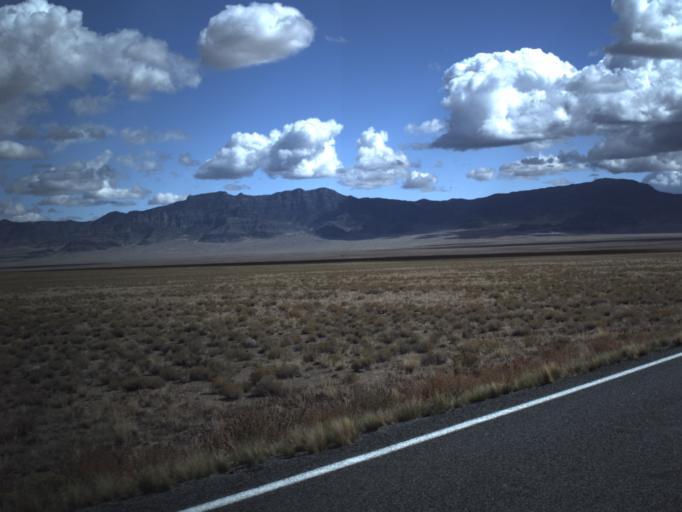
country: US
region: Utah
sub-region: Beaver County
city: Milford
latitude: 38.5601
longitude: -113.7570
